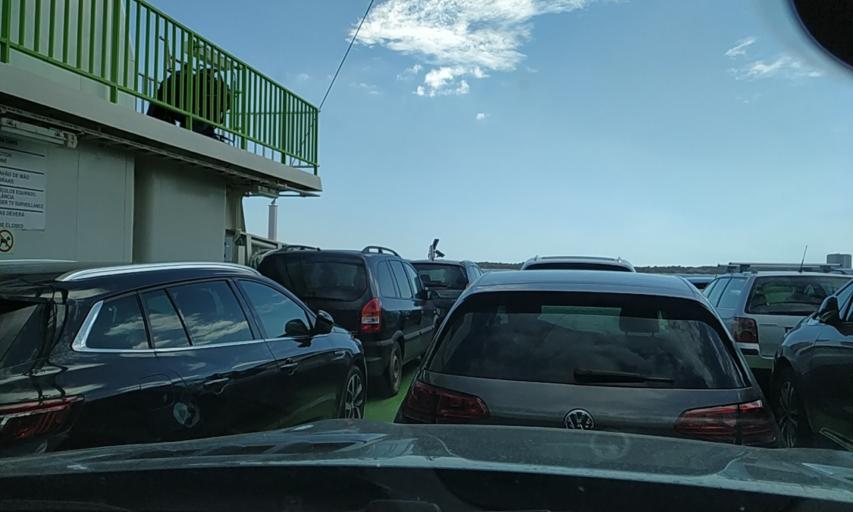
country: PT
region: Setubal
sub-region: Setubal
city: Setubal
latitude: 38.5029
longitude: -8.8860
